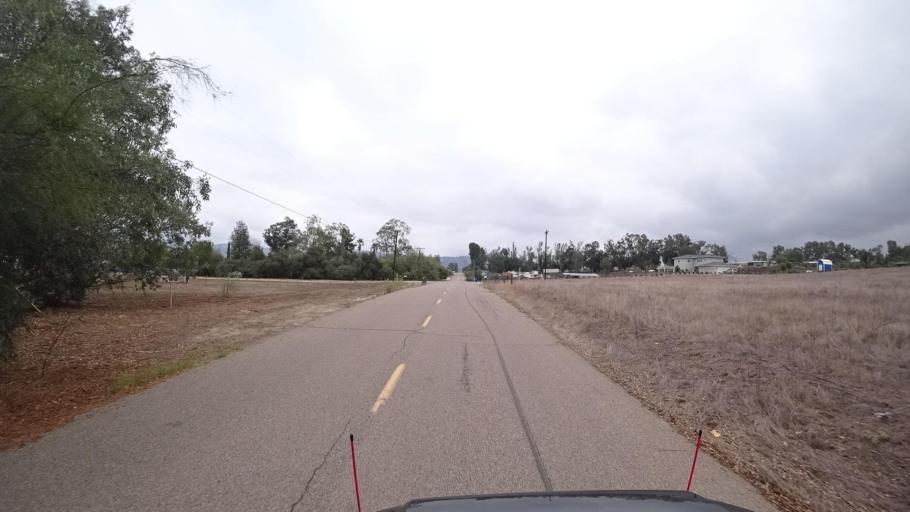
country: US
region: California
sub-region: San Diego County
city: Ramona
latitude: 33.0584
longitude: -116.8680
